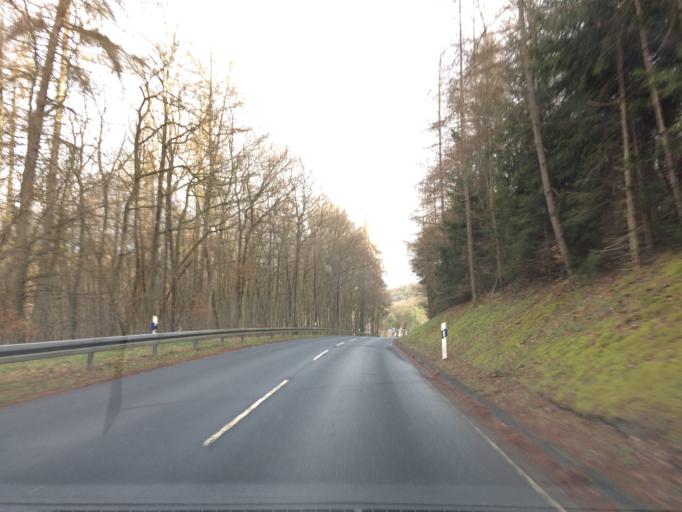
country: DE
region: Hesse
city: Weilmunster
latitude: 50.3672
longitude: 8.3868
